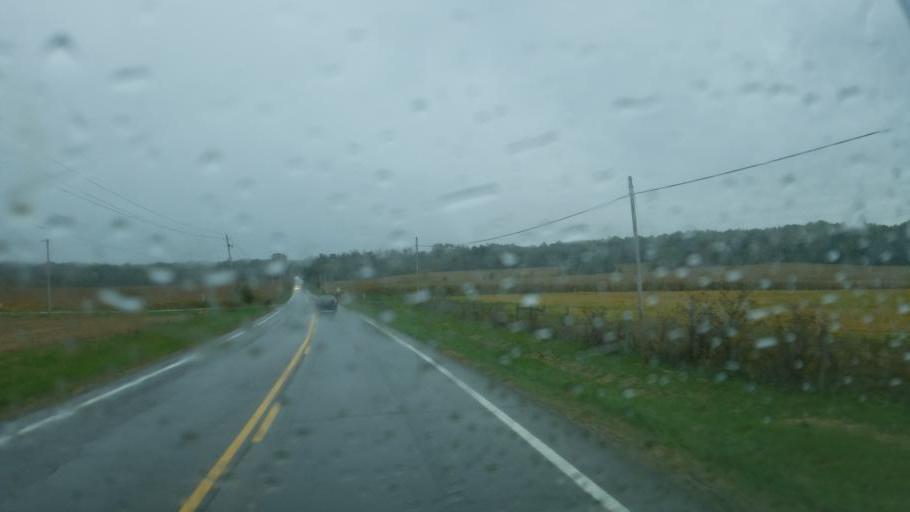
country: US
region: Ohio
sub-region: Richland County
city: Lincoln Heights
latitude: 40.8376
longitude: -82.4773
